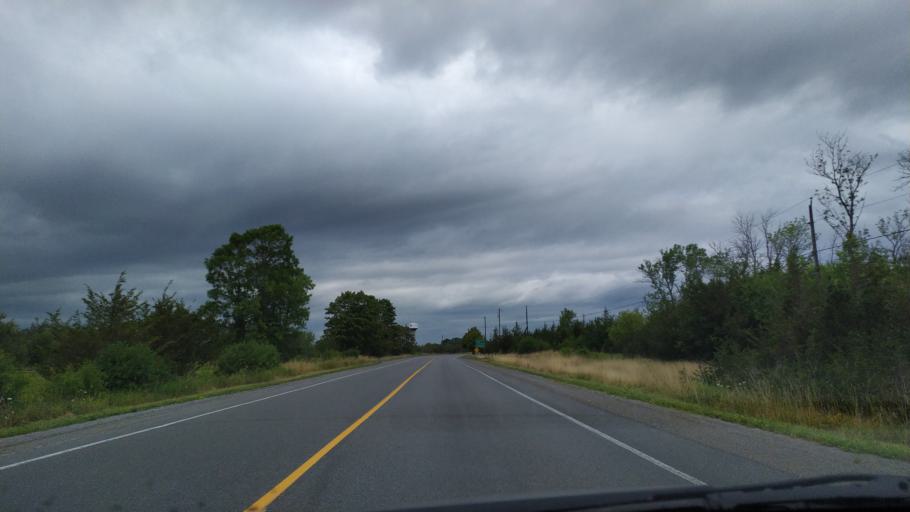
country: CA
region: Ontario
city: Quinte West
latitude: 43.9839
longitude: -77.5140
